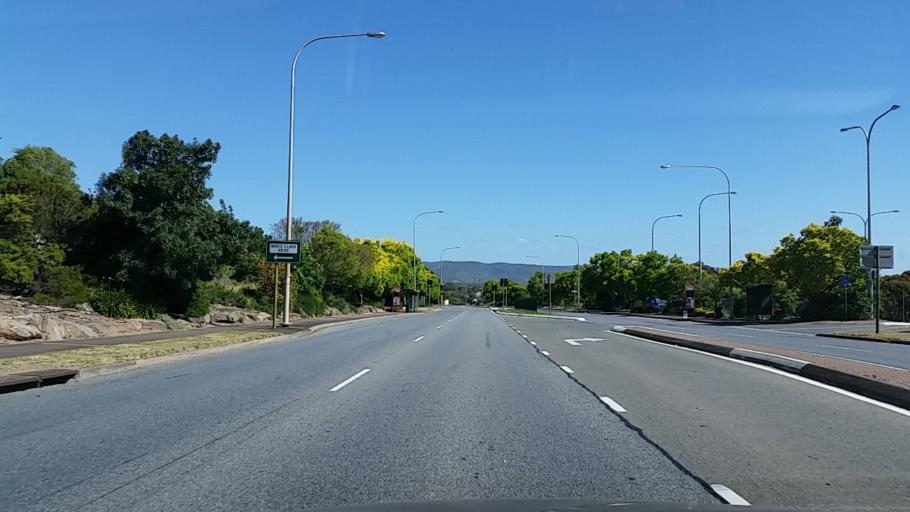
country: AU
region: South Australia
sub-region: Tea Tree Gully
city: Golden Grove
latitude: -34.7915
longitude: 138.6978
